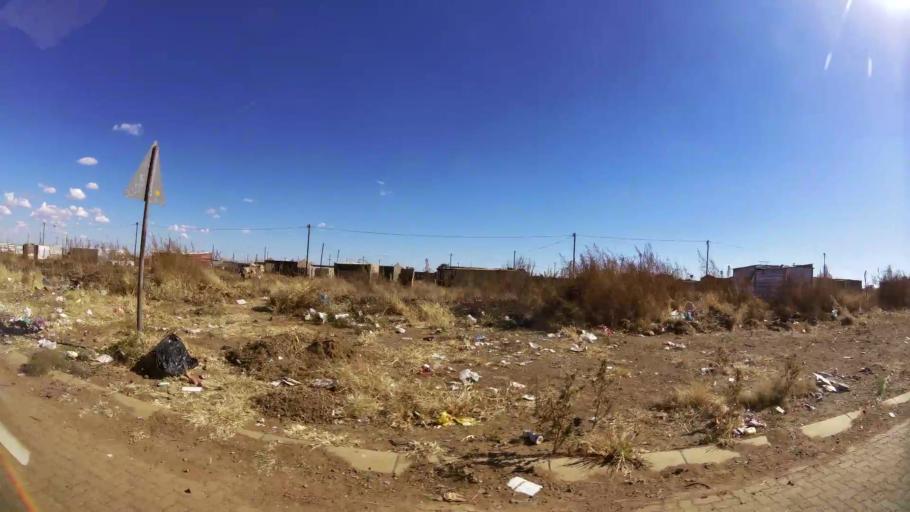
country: ZA
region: North-West
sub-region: Dr Kenneth Kaunda District Municipality
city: Klerksdorp
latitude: -26.8664
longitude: 26.5654
